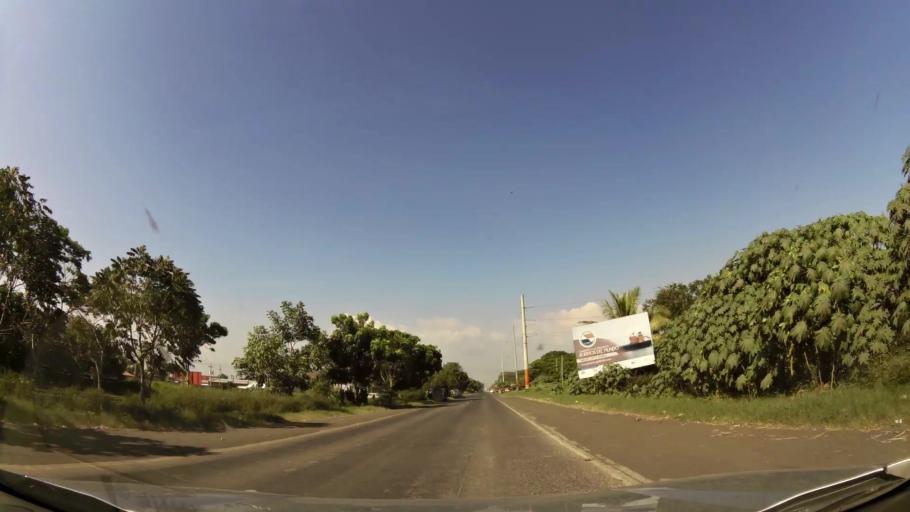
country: GT
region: Escuintla
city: Puerto San Jose
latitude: 13.9408
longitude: -90.7885
